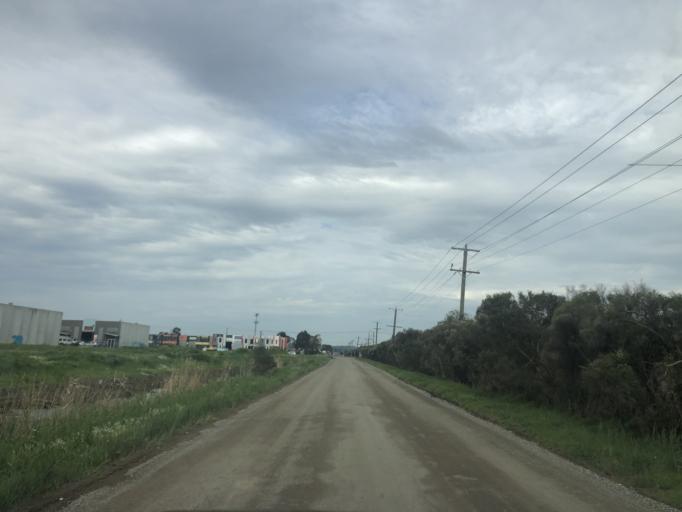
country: AU
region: Victoria
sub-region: Casey
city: Hallam
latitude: -38.0195
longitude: 145.2676
